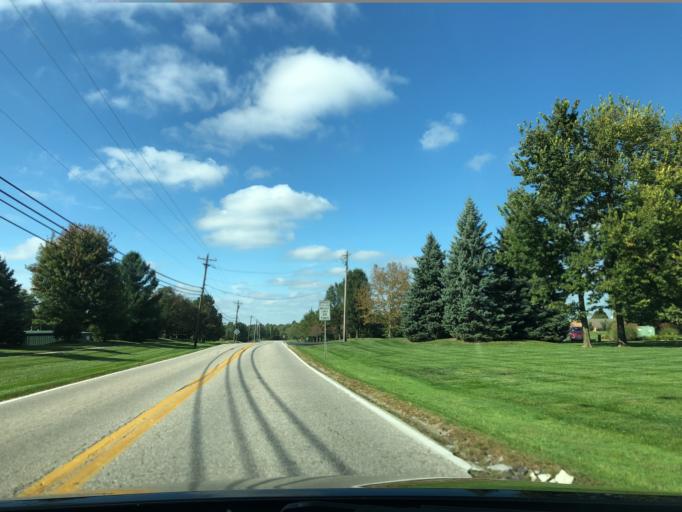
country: US
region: Ohio
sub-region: Hamilton County
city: Loveland
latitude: 39.2373
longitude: -84.2438
